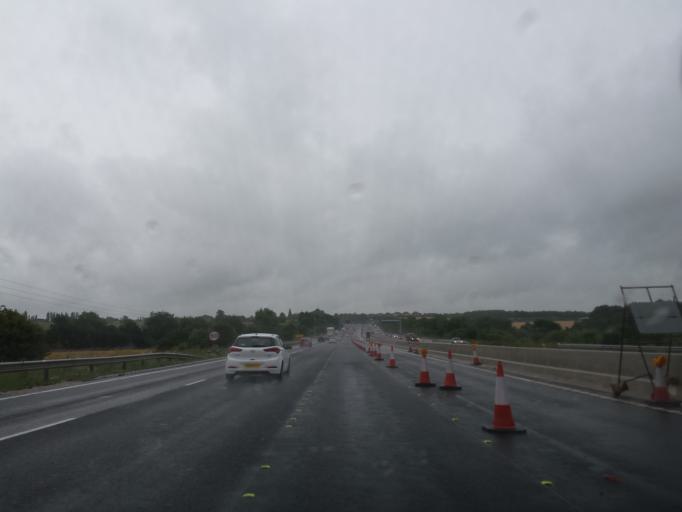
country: GB
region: England
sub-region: Rotherham
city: Wales
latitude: 53.3515
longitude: -1.2867
